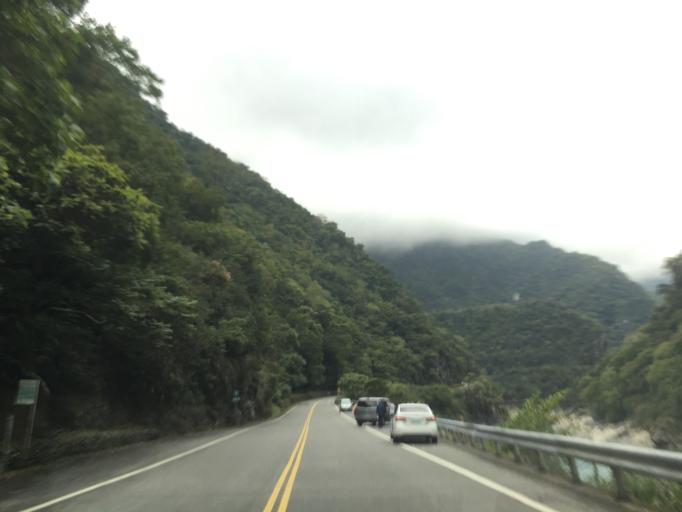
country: TW
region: Taiwan
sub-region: Hualien
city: Hualian
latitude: 24.1762
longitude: 121.5836
